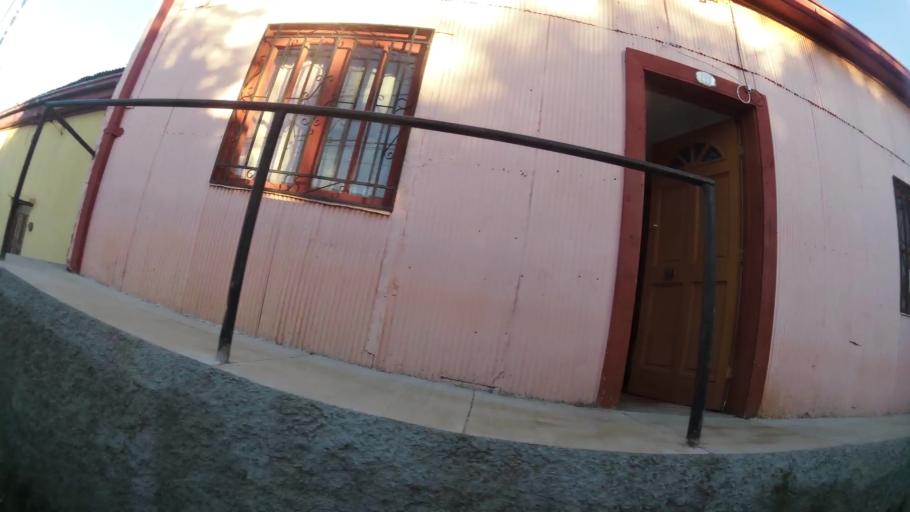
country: CL
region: Valparaiso
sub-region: Provincia de Valparaiso
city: Valparaiso
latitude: -33.0567
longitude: -71.6050
